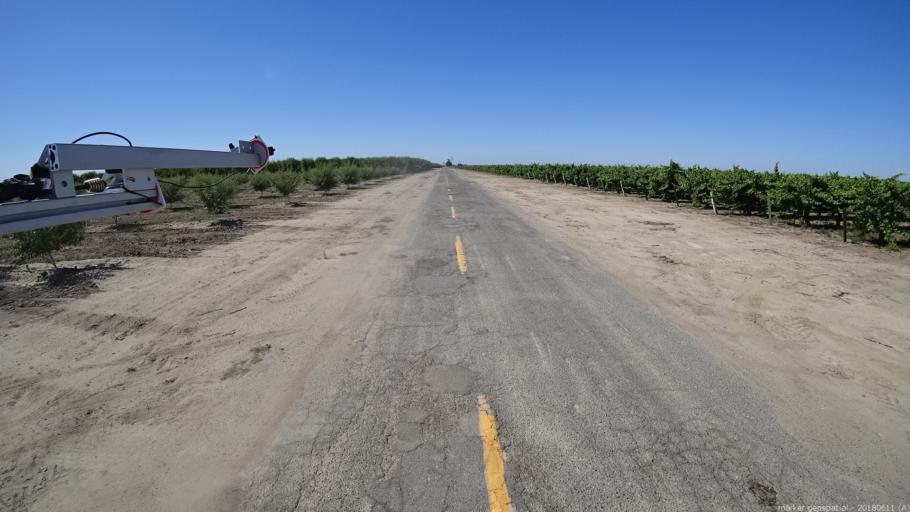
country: US
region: California
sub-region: Madera County
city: Madera
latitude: 36.9592
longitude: -120.1659
